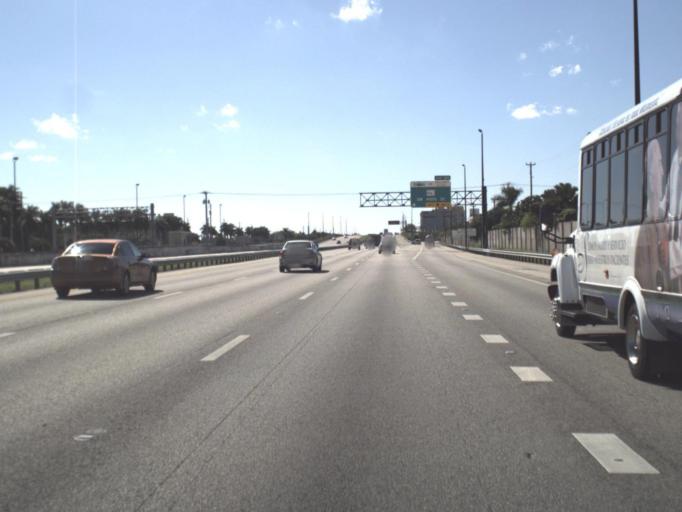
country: US
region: Florida
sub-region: Miami-Dade County
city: Westwood Lake
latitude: 25.7391
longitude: -80.3847
